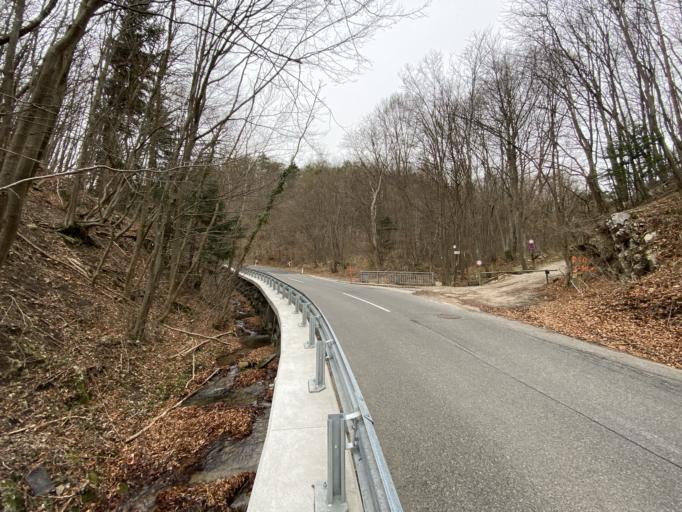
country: AT
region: Lower Austria
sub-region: Politischer Bezirk Modling
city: Gaaden
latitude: 48.0218
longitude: 16.1902
